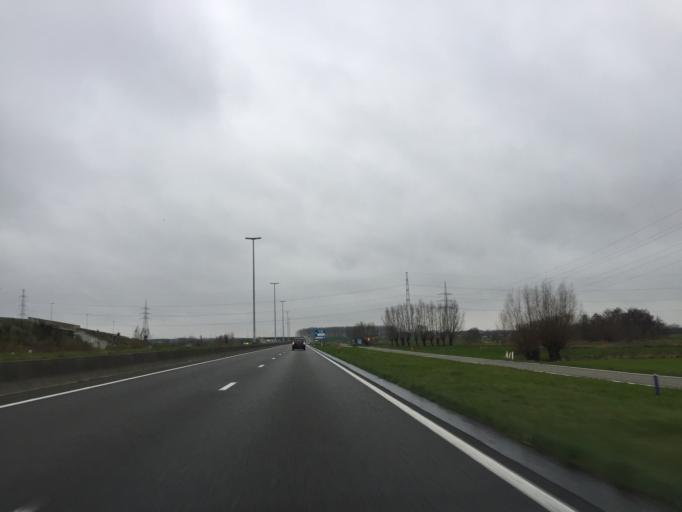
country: BE
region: Flanders
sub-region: Provincie Oost-Vlaanderen
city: Evergem
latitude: 51.1507
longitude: 3.7439
